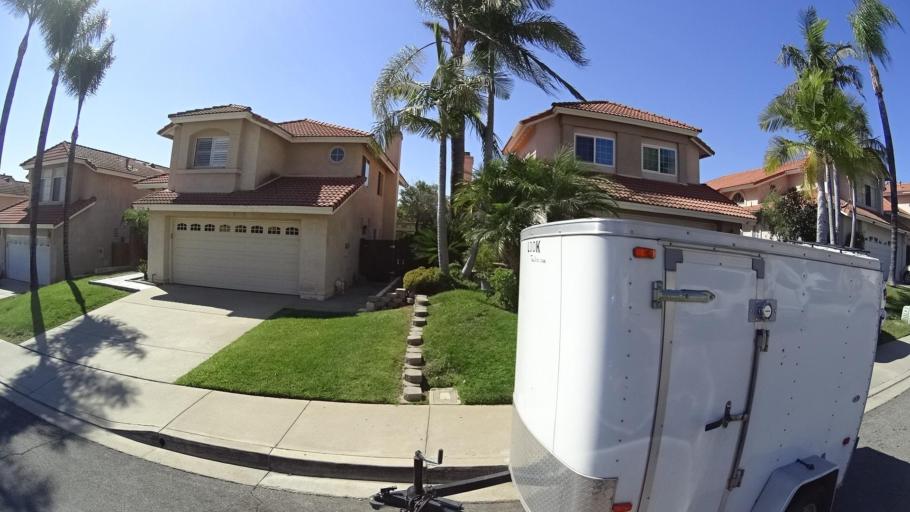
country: US
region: California
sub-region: San Diego County
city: Rancho San Diego
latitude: 32.7515
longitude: -116.9346
